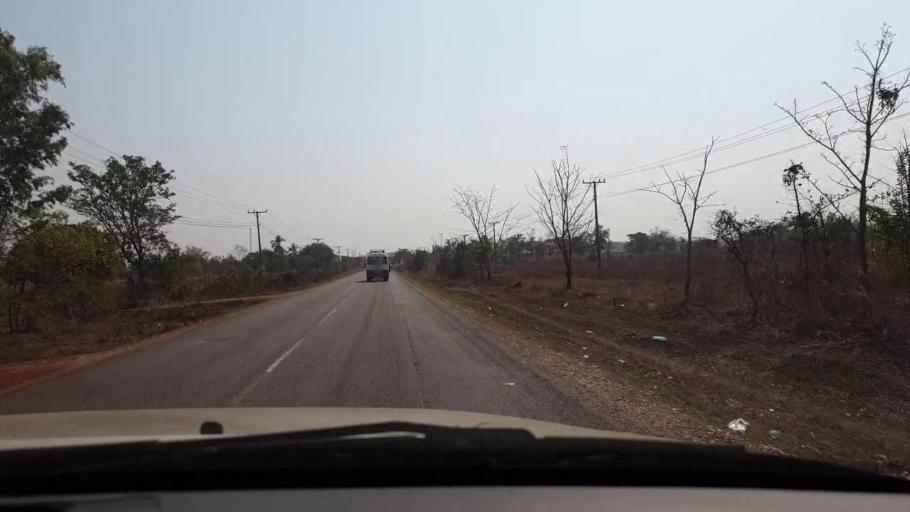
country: TH
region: Nong Khai
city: Nong Khai
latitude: 18.0554
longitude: 102.8306
